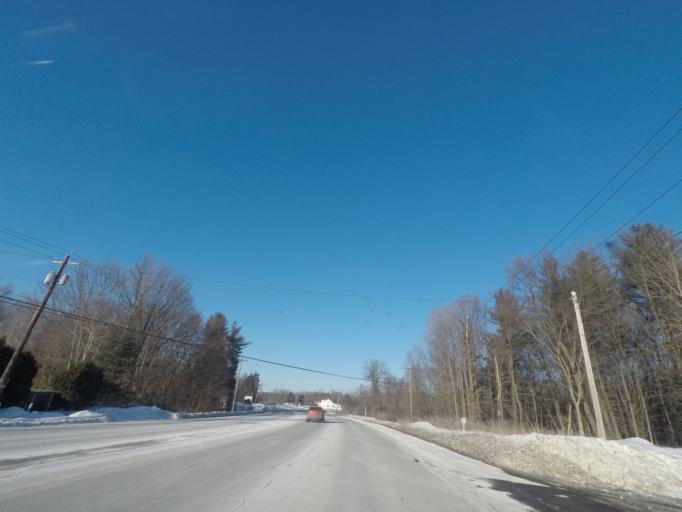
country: US
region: New York
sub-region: Saratoga County
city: Ballston Spa
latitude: 42.9801
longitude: -73.7873
